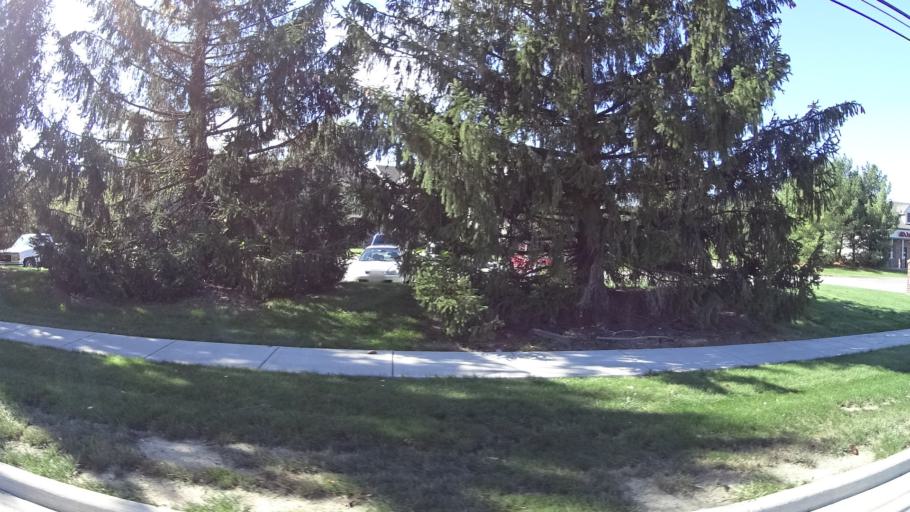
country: US
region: Ohio
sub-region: Lorain County
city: Grafton
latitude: 41.2790
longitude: -82.0629
